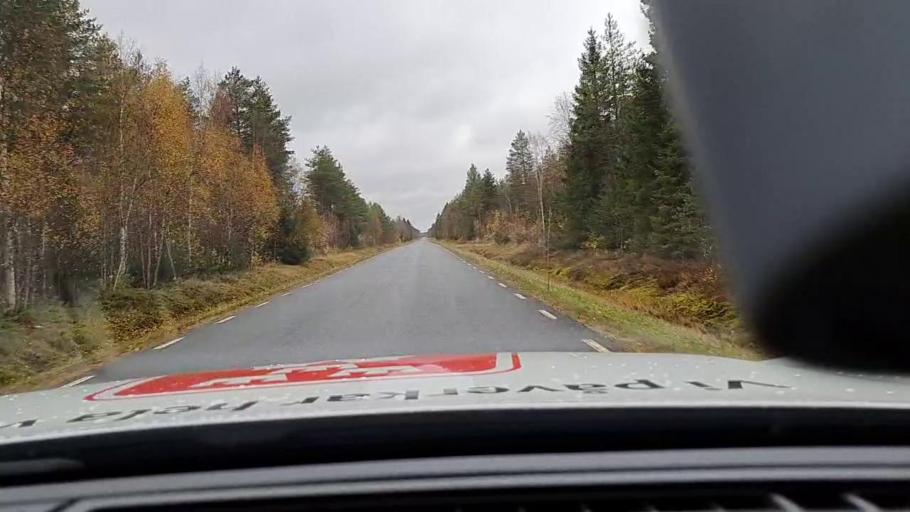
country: SE
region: Norrbotten
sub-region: Haparanda Kommun
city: Haparanda
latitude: 65.9101
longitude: 23.8299
